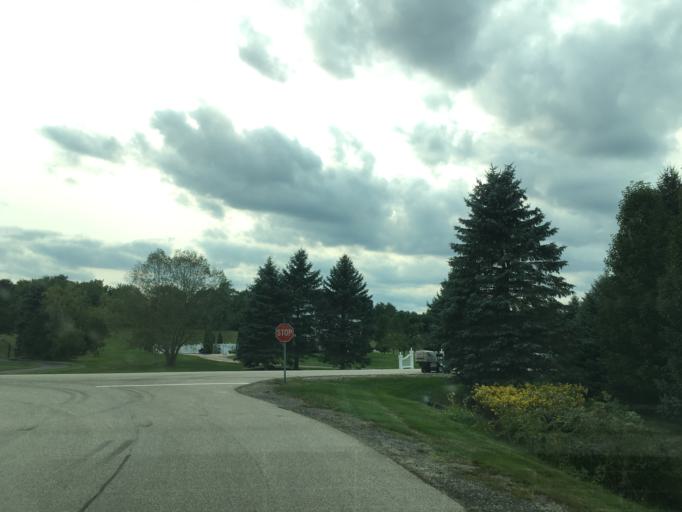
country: US
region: New Hampshire
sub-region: Rockingham County
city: Stratham Station
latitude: 43.0035
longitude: -70.8912
